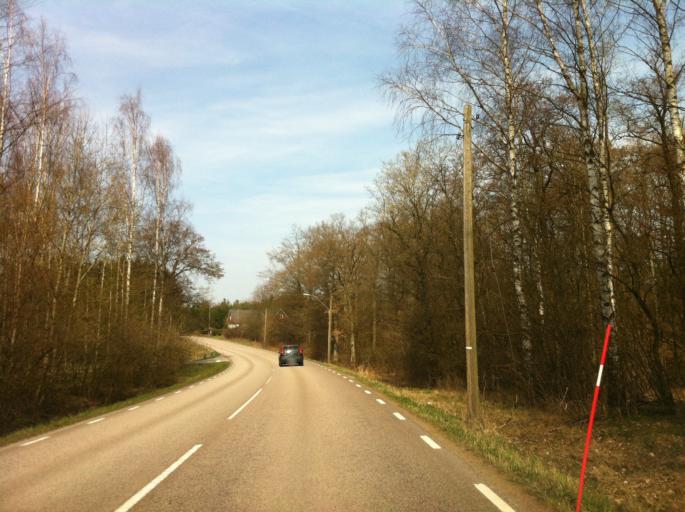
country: SE
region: Skane
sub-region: Svalovs Kommun
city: Svaloev
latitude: 55.9509
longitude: 13.1104
